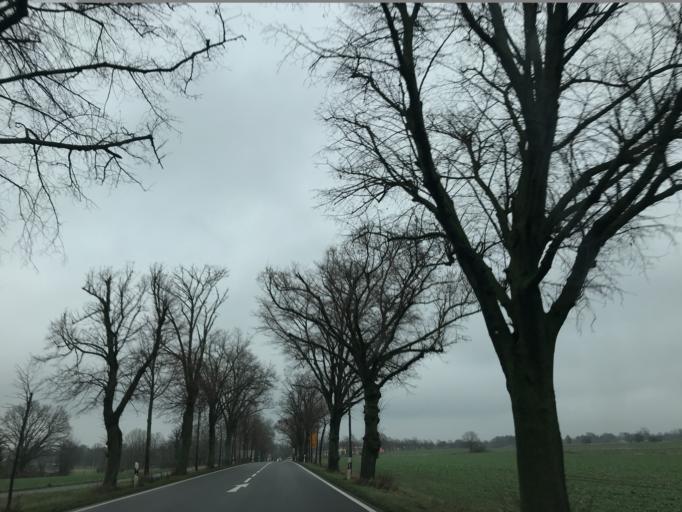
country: DE
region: Brandenburg
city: Kremmen
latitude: 52.7548
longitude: 13.0171
